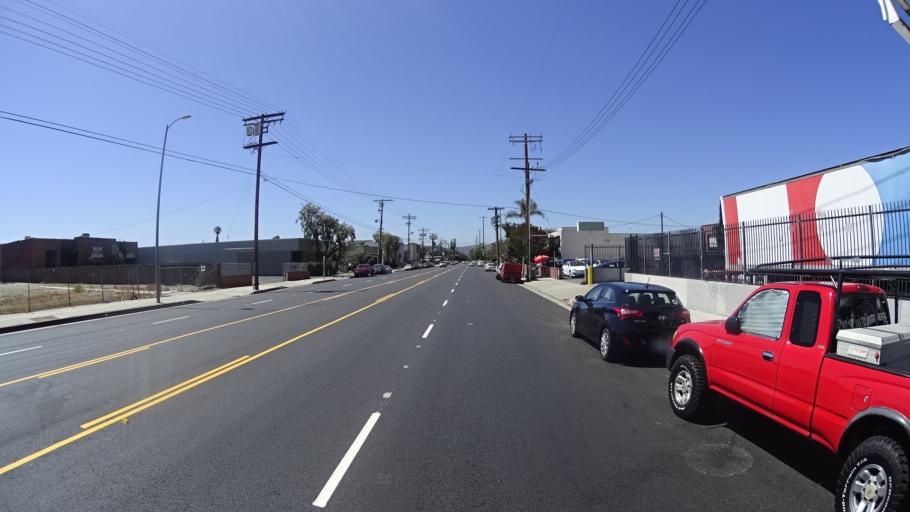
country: US
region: California
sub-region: Los Angeles County
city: Van Nuys
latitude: 34.1970
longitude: -118.4925
